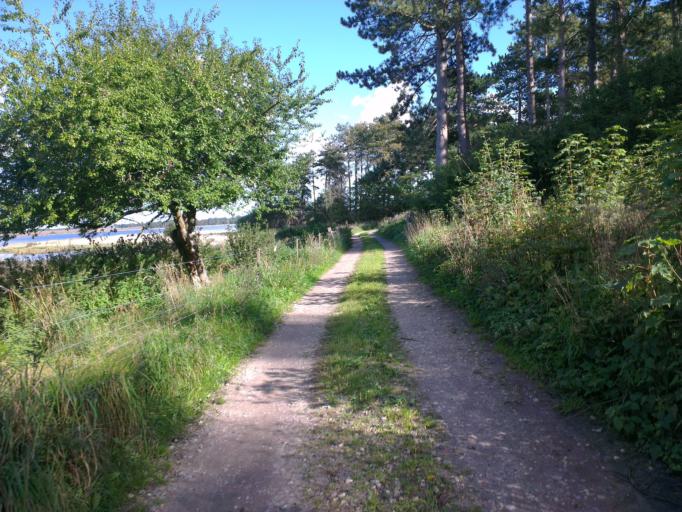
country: DK
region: Capital Region
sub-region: Frederikssund Kommune
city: Frederikssund
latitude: 55.7966
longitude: 12.0551
